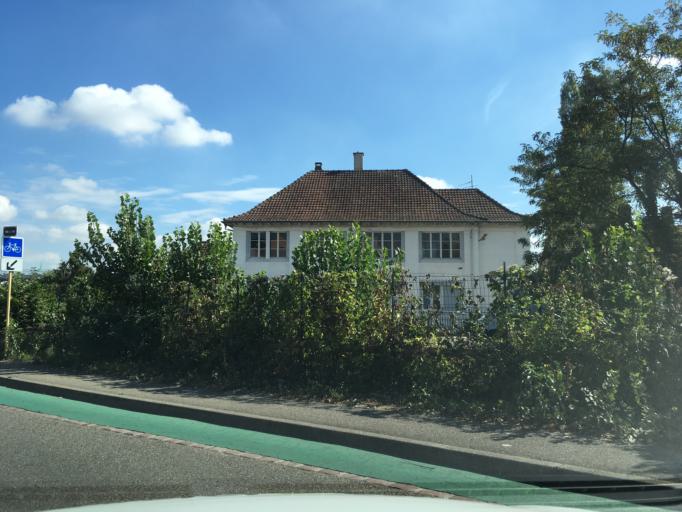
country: FR
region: Alsace
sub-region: Departement du Haut-Rhin
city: Colmar
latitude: 48.0711
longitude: 7.3429
